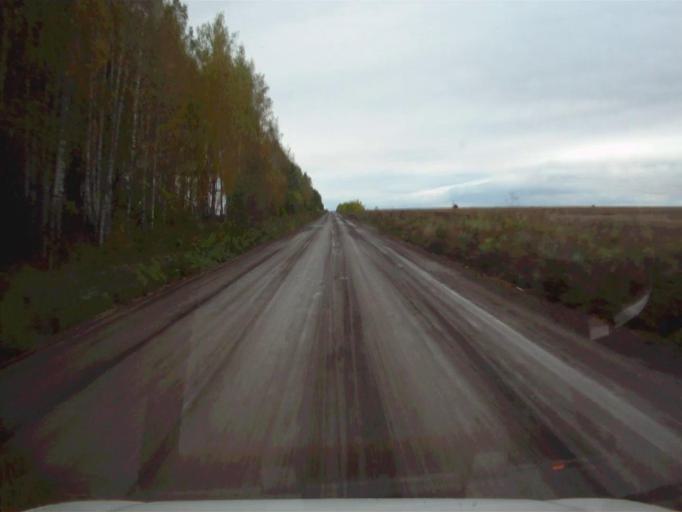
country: RU
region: Sverdlovsk
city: Mikhaylovsk
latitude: 56.1519
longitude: 59.2669
